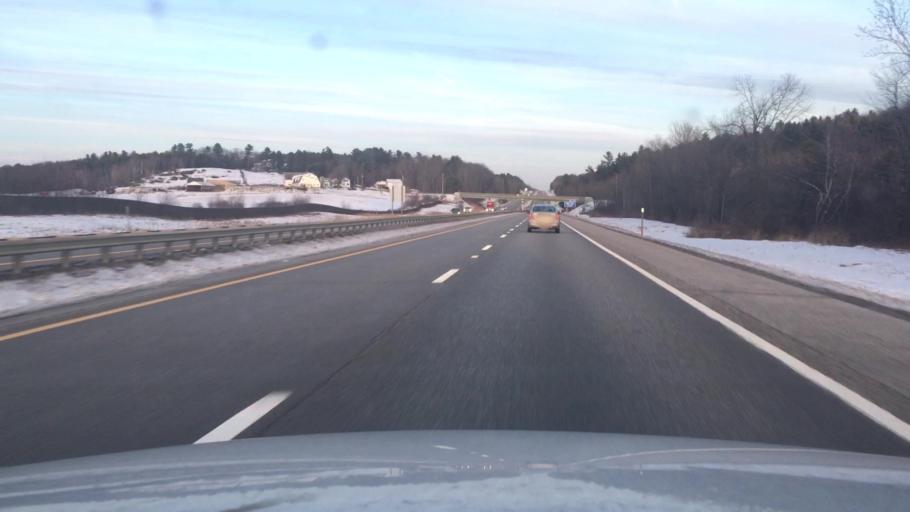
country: US
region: Maine
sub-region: Androscoggin County
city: Sabattus
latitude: 44.1104
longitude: -70.0671
